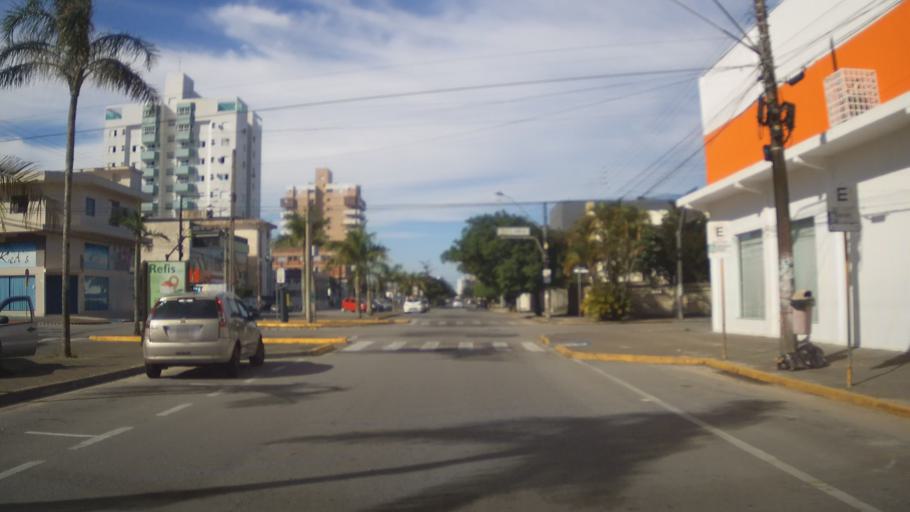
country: BR
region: Sao Paulo
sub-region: Itanhaem
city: Itanhaem
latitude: -24.1843
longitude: -46.7869
